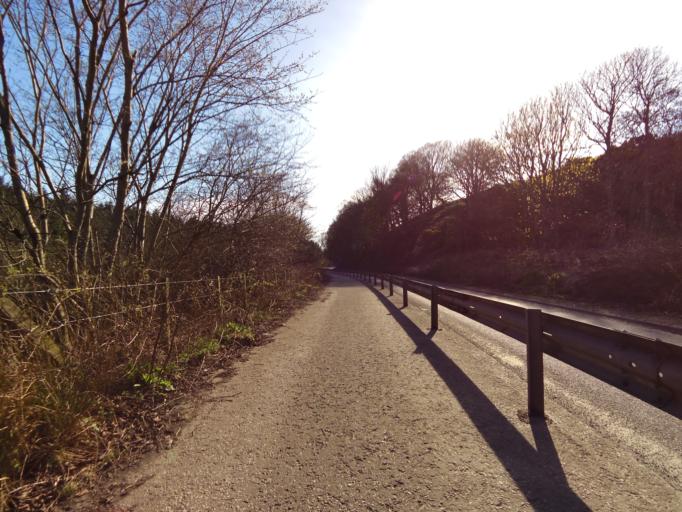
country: GB
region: Scotland
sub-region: Aberdeenshire
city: Stonehaven
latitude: 56.9831
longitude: -2.1883
